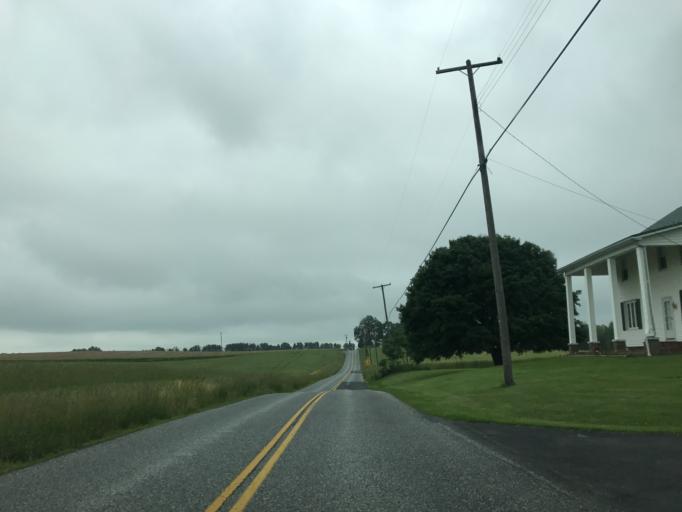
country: US
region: Pennsylvania
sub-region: York County
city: Susquehanna Trails
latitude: 39.7114
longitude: -76.4518
